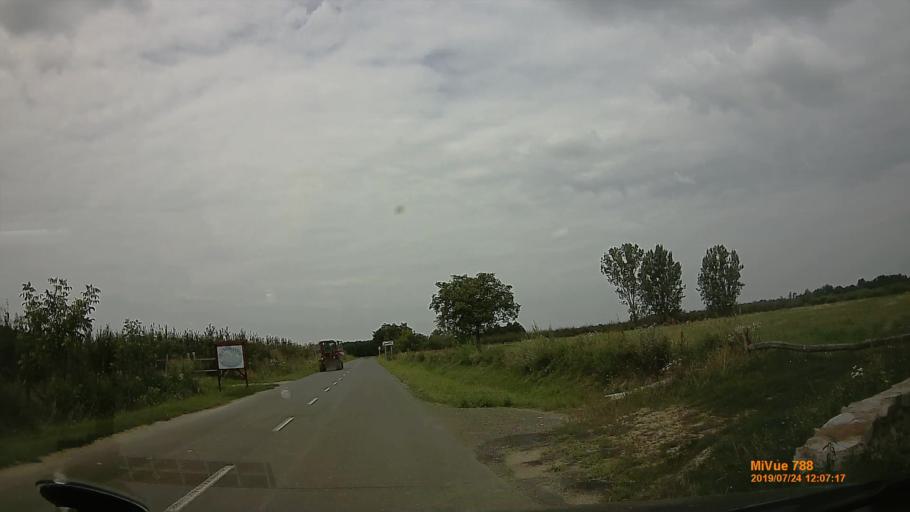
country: HU
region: Szabolcs-Szatmar-Bereg
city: Vasarosnameny
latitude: 48.1921
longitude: 22.3955
